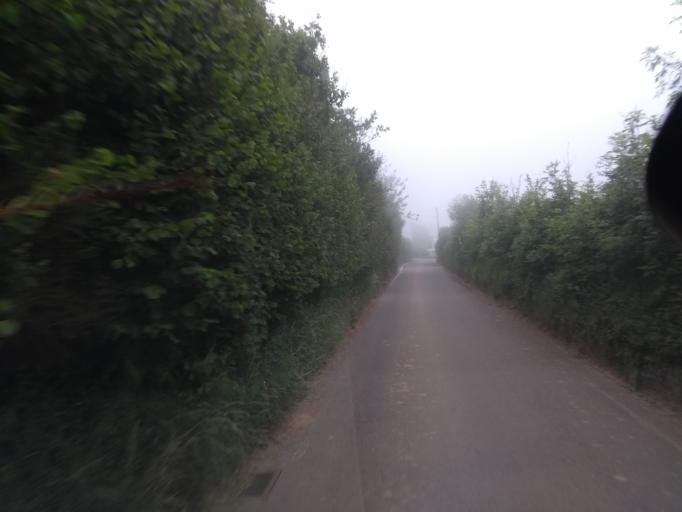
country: GB
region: England
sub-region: Dorset
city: Bridport
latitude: 50.7783
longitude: -2.7761
